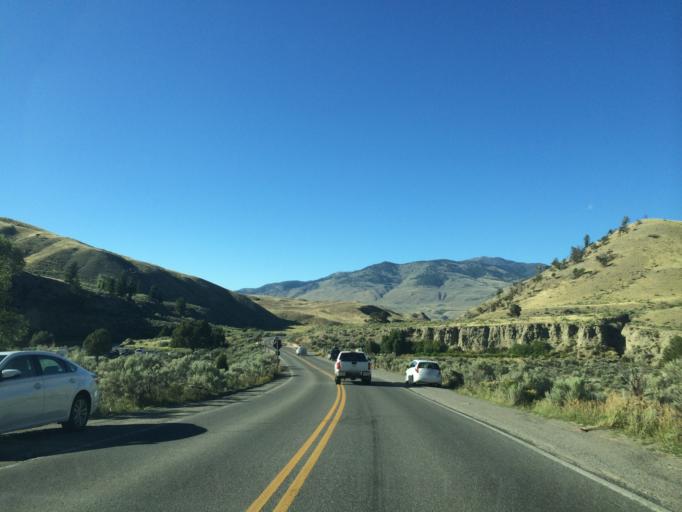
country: US
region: Montana
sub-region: Gallatin County
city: West Yellowstone
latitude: 44.9918
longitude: -110.6921
